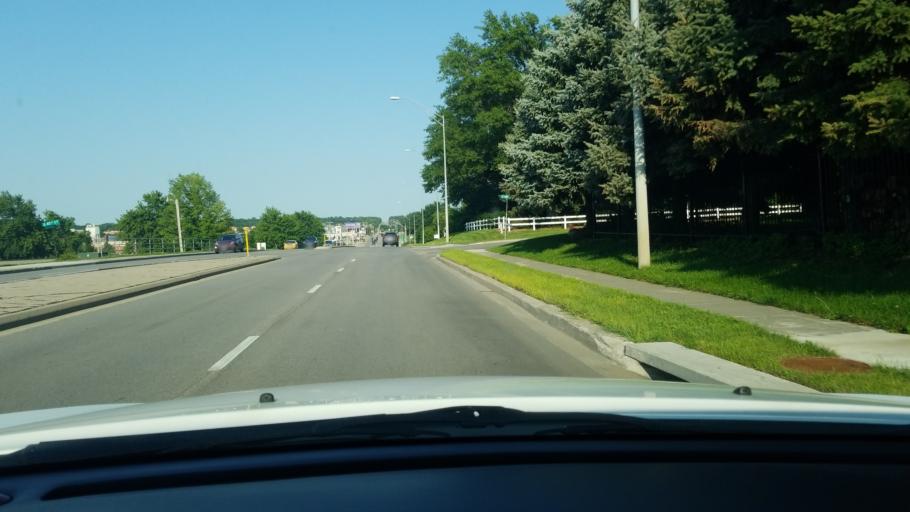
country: US
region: Nebraska
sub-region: Lancaster County
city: Lincoln
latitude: 40.7552
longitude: -96.6574
